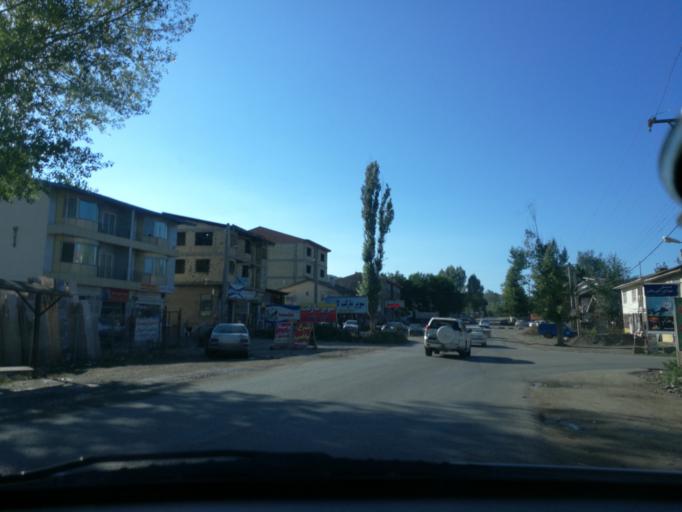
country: IR
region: Mazandaran
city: `Abbasabad
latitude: 36.5382
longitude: 51.1804
